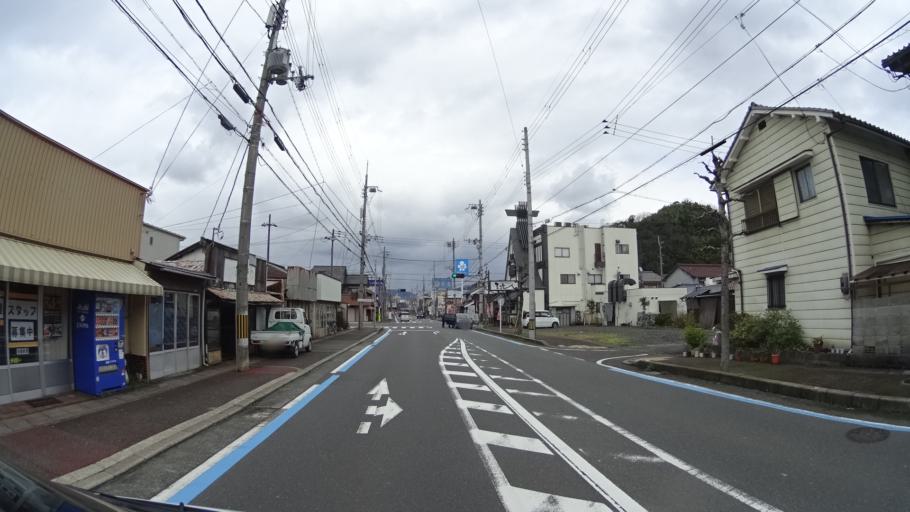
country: JP
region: Kyoto
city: Maizuru
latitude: 35.4673
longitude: 135.3974
